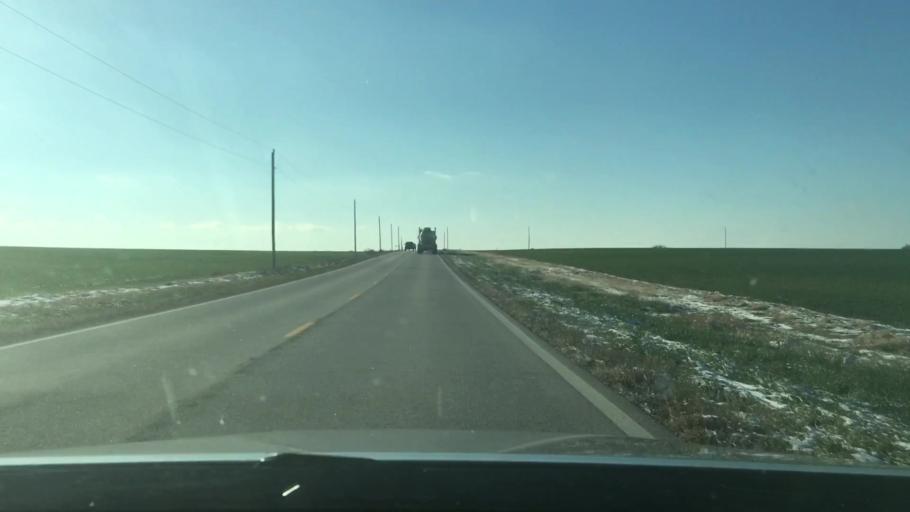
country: US
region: Kansas
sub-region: Reno County
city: Nickerson
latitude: 38.1450
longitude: -98.1566
